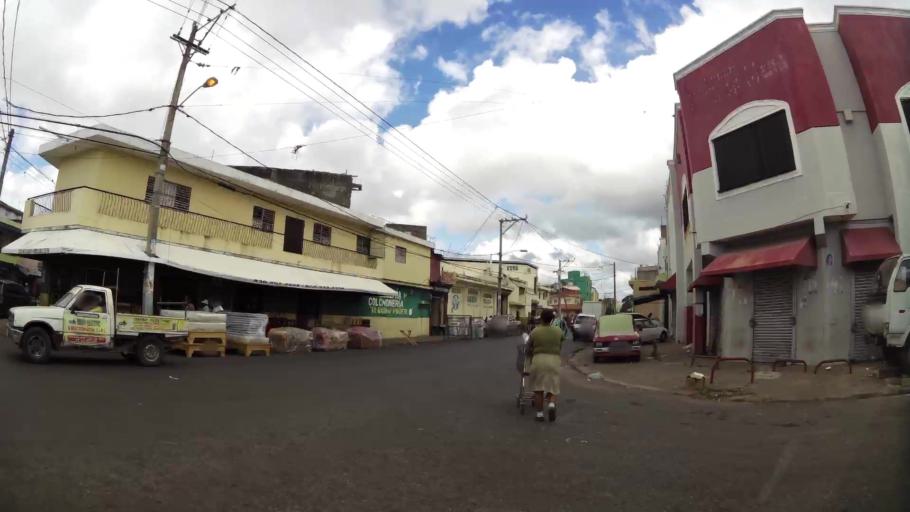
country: DO
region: Nacional
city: San Carlos
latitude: 18.4891
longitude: -69.8980
